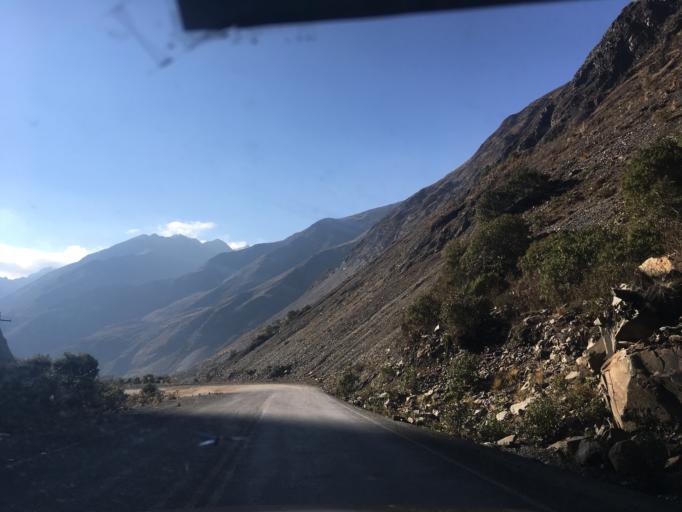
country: BO
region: La Paz
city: Quime
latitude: -17.0011
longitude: -67.2810
